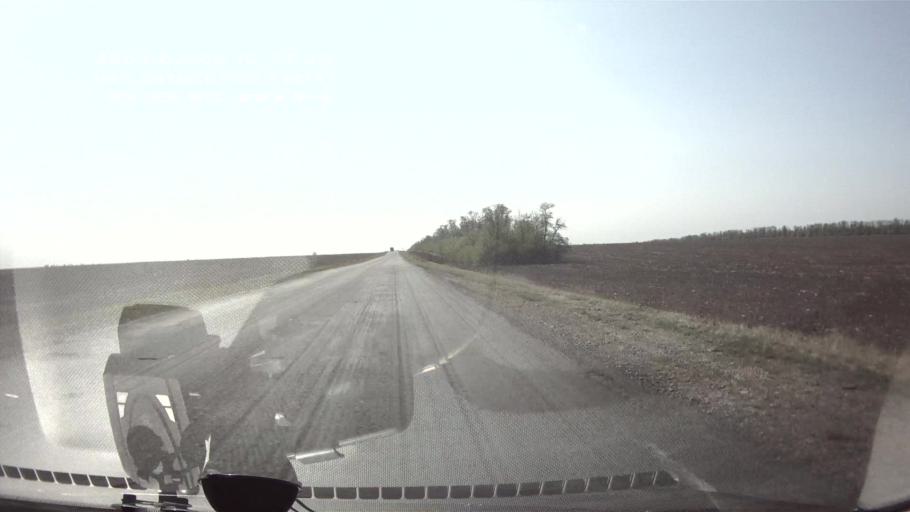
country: RU
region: Krasnodarskiy
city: Dmitriyevskaya
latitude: 45.6894
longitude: 40.7440
